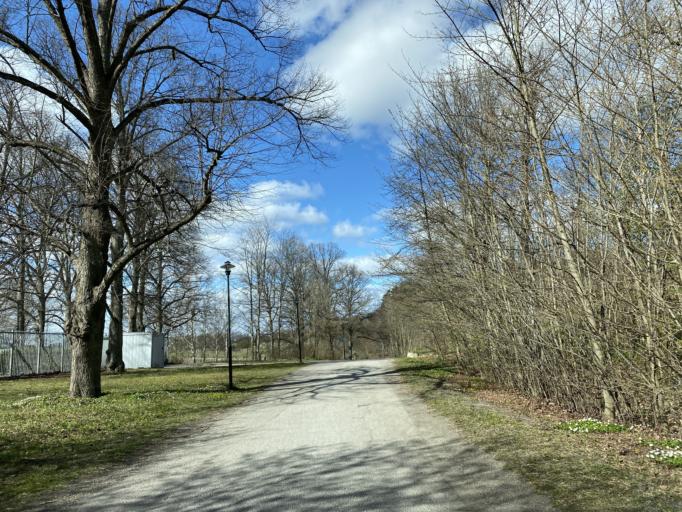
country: SE
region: Stockholm
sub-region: Lidingo
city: Lidingoe
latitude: 59.3323
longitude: 18.1248
